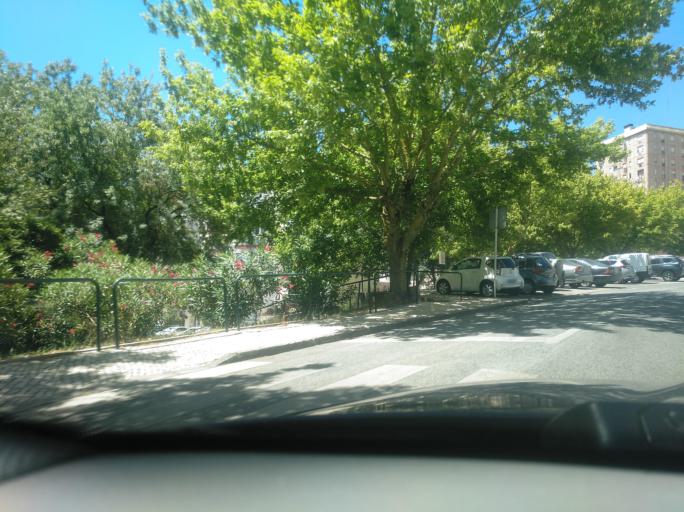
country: PT
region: Lisbon
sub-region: Odivelas
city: Povoa de Santo Adriao
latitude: 38.8112
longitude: -9.1593
